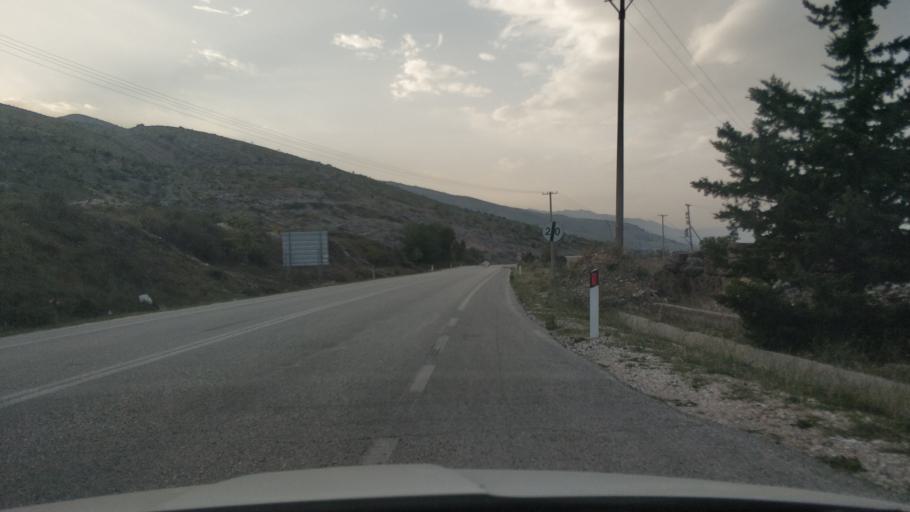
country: AL
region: Gjirokaster
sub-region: Rrethi i Gjirokastres
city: Libohove
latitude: 39.9433
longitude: 20.2645
